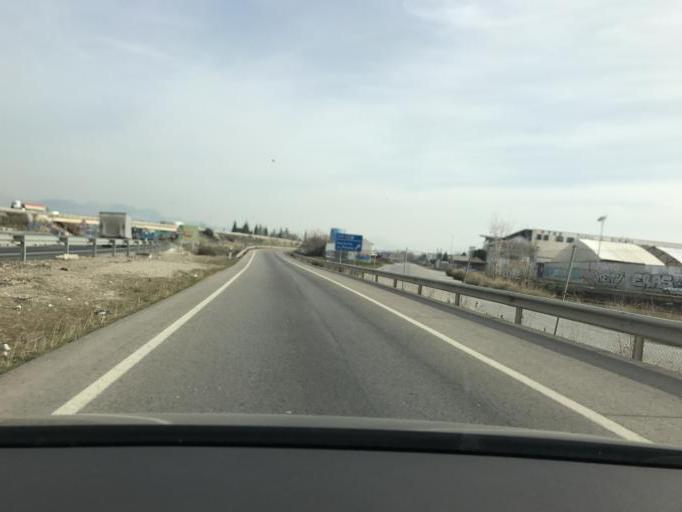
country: ES
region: Andalusia
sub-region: Provincia de Granada
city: Chauchina
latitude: 37.1905
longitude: -3.7411
